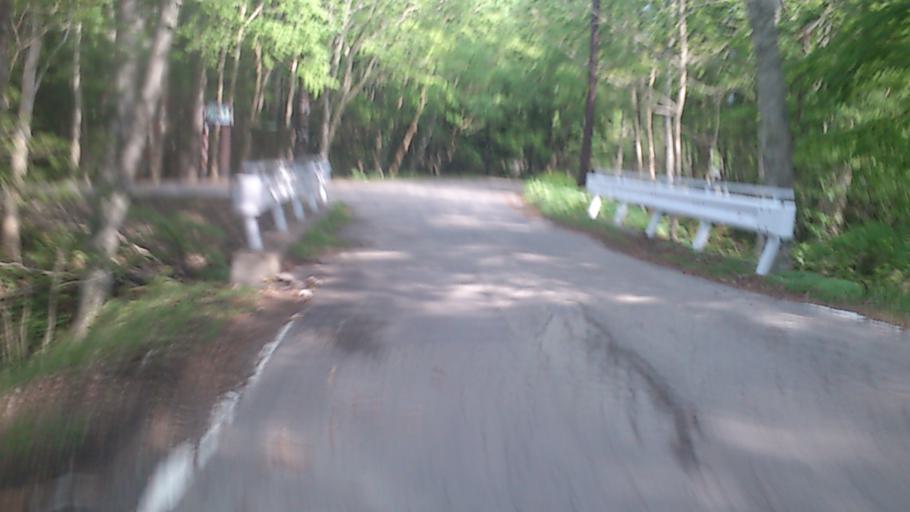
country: JP
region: Hokkaido
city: Kitami
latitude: 43.3812
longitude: 143.9704
